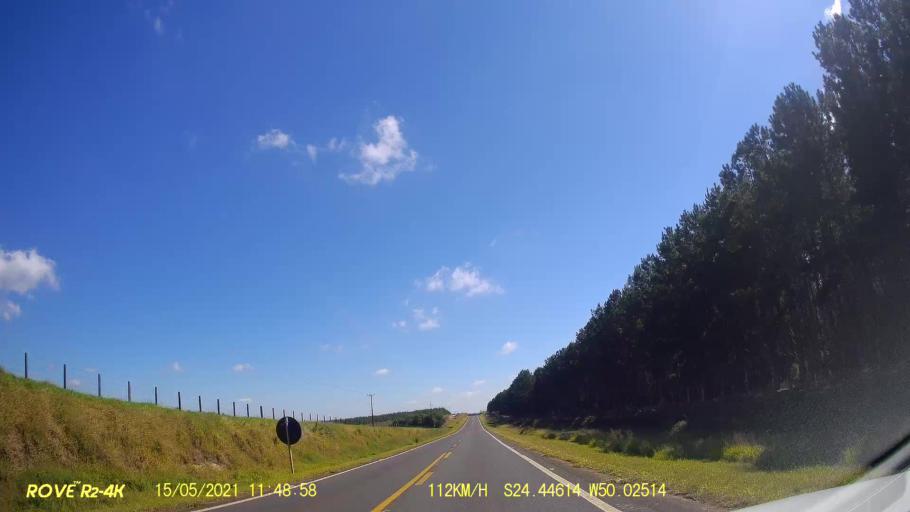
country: BR
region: Parana
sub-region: Pirai Do Sul
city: Pirai do Sul
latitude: -24.4465
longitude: -50.0248
